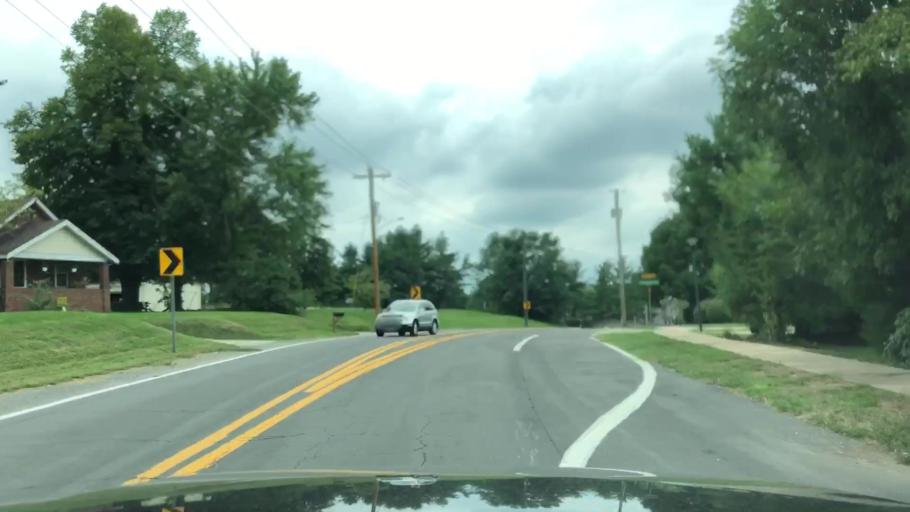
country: US
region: Missouri
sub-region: Saint Louis County
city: Hazelwood
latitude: 38.8099
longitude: -90.3796
